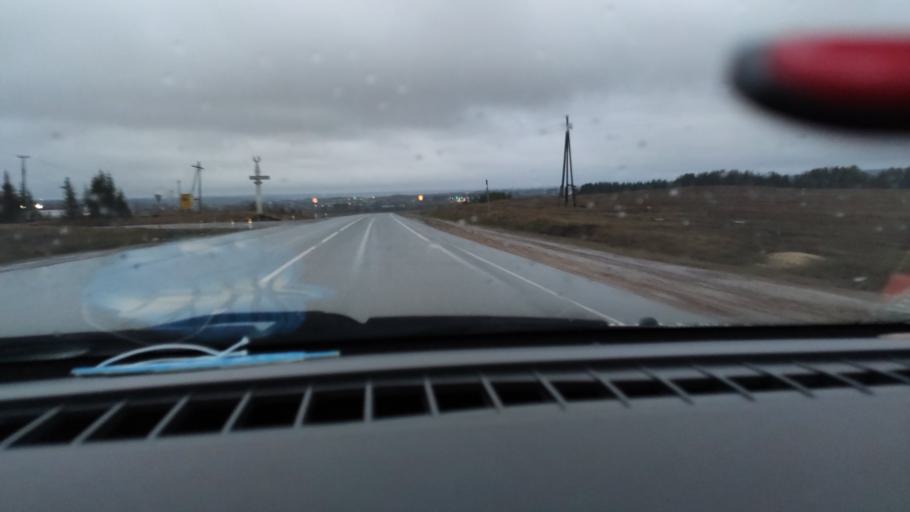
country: RU
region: Udmurtiya
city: Alnashi
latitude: 56.1938
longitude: 52.4557
